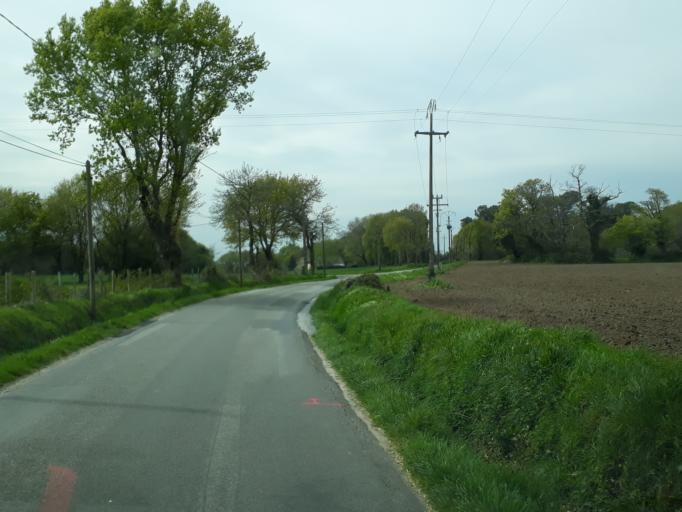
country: FR
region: Brittany
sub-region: Departement du Morbihan
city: Theix
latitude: 47.6500
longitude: -2.6323
